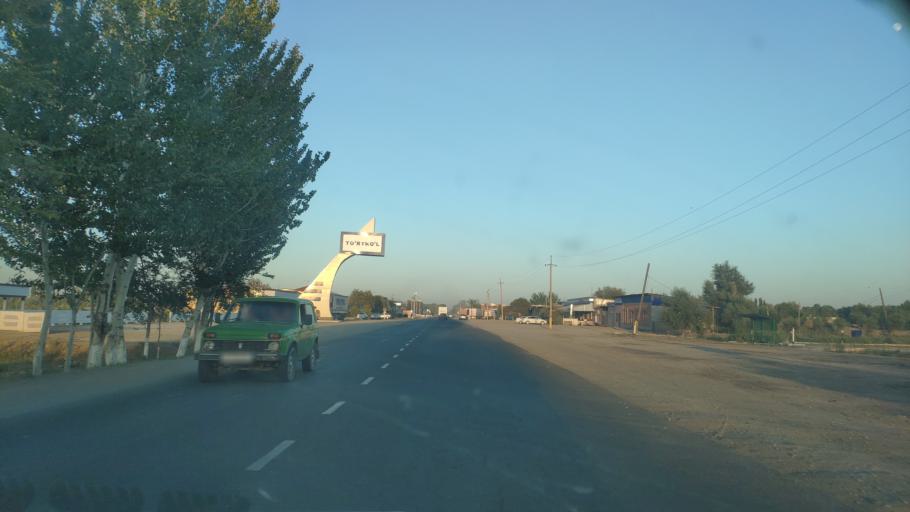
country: UZ
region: Karakalpakstan
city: To'rtko'l Shahri
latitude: 41.5691
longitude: 60.9479
